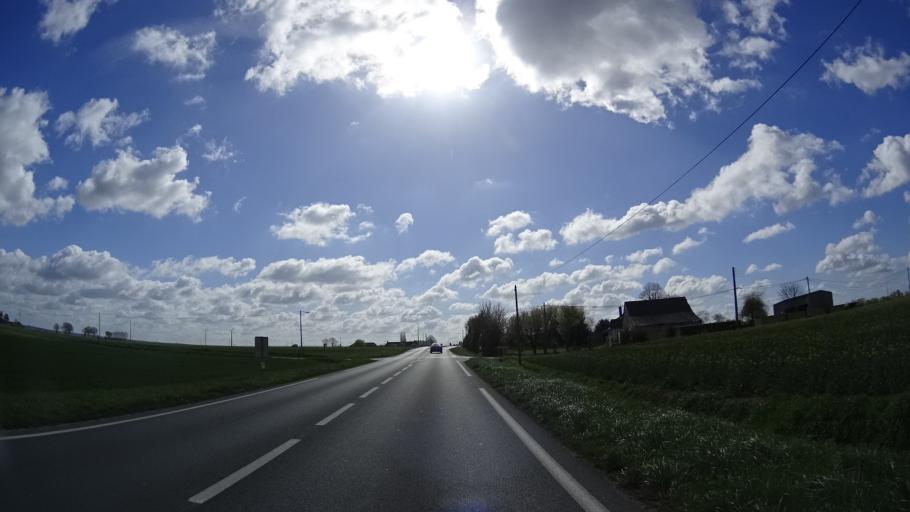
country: FR
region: Pays de la Loire
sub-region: Departement de Maine-et-Loire
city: Brissac-Quince
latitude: 47.3282
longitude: -0.4192
